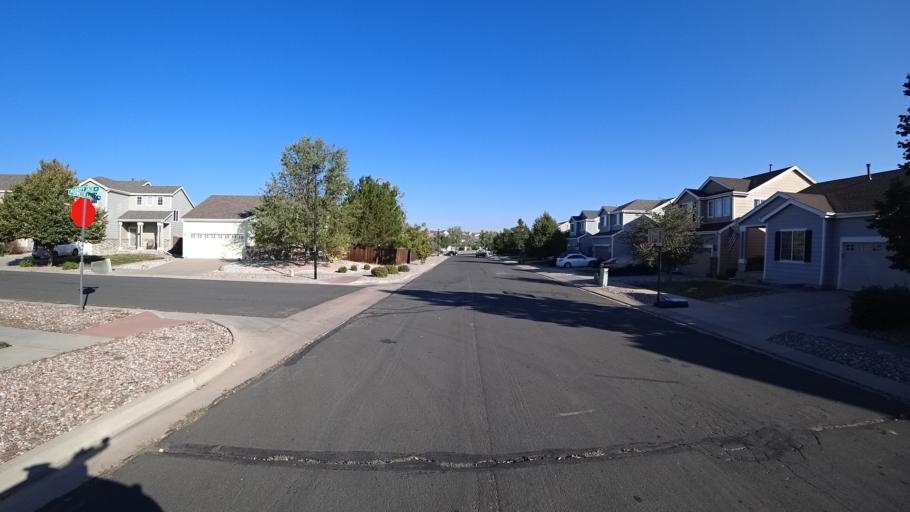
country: US
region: Colorado
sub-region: El Paso County
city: Cimarron Hills
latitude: 38.8890
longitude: -104.6934
